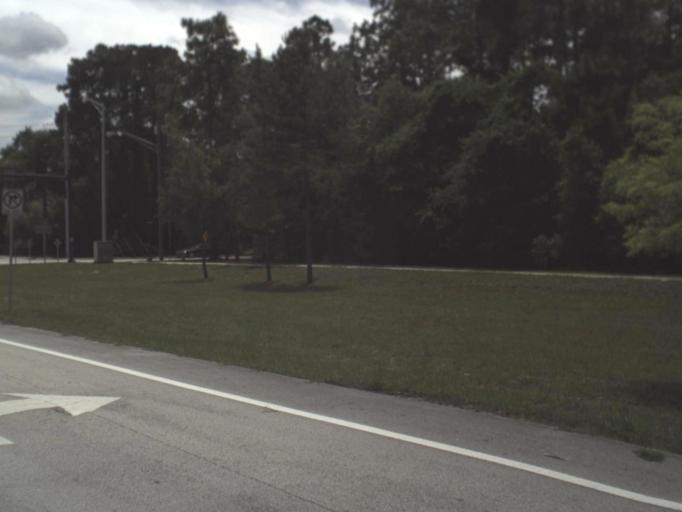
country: US
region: Florida
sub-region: Saint Johns County
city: Fruit Cove
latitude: 30.2107
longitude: -81.5520
